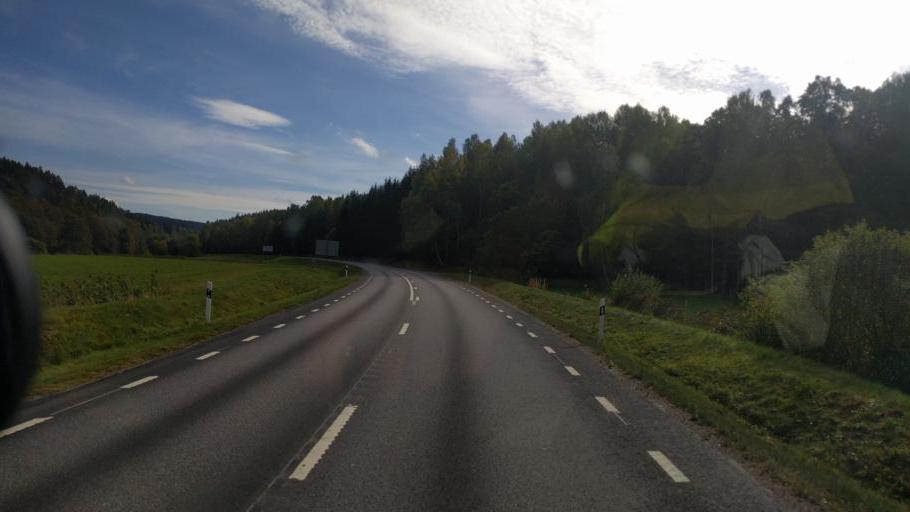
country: SE
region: OEstergoetland
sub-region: Kinda Kommun
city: Kisa
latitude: 57.9751
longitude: 15.6433
